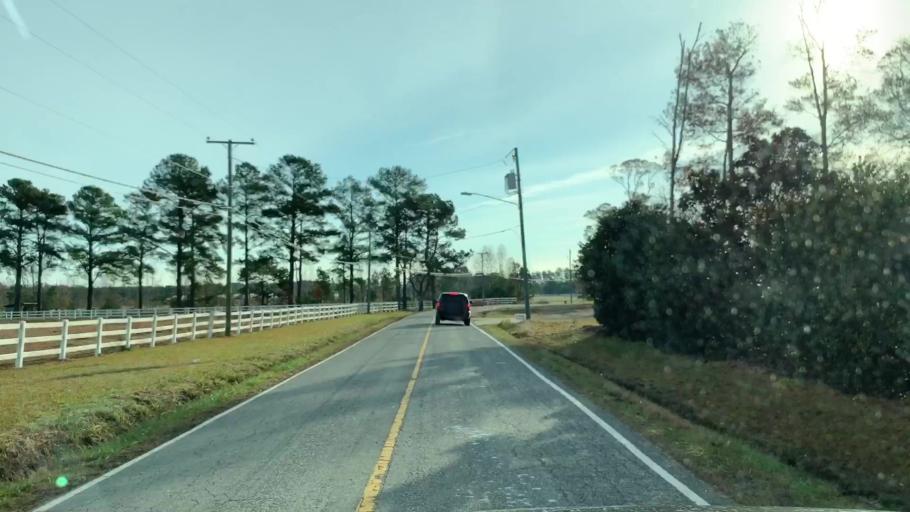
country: US
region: Virginia
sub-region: City of Virginia Beach
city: Virginia Beach
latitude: 36.6883
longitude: -76.0022
